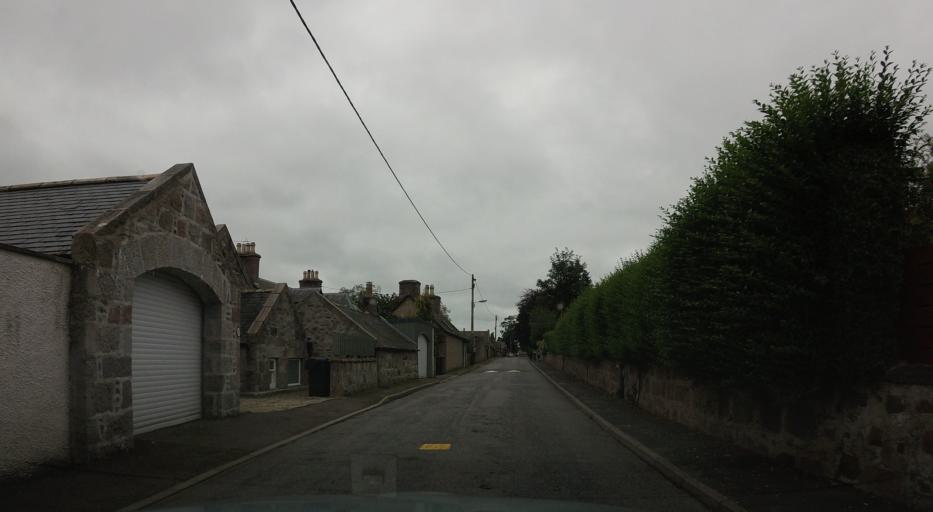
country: GB
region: Scotland
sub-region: Aberdeenshire
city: Banchory
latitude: 57.0517
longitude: -2.4958
